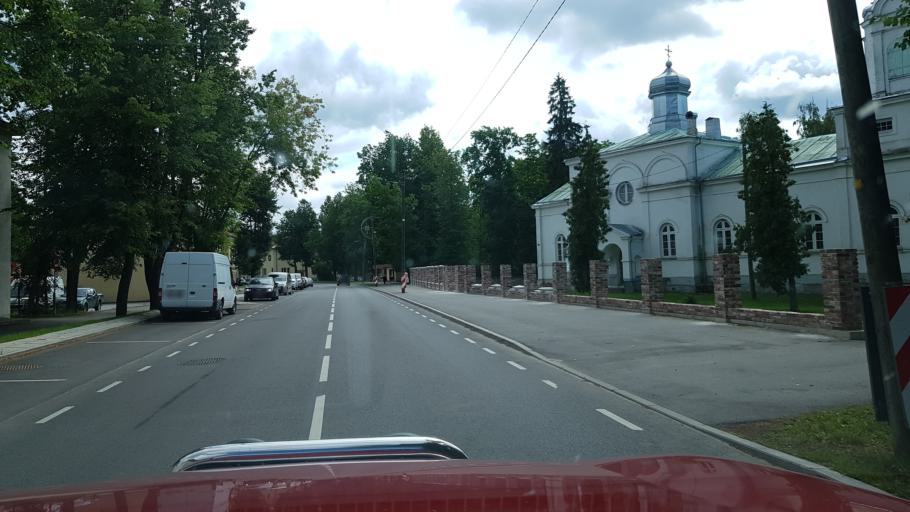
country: EE
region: Jogevamaa
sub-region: Mustvee linn
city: Mustvee
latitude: 58.8482
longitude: 26.9406
